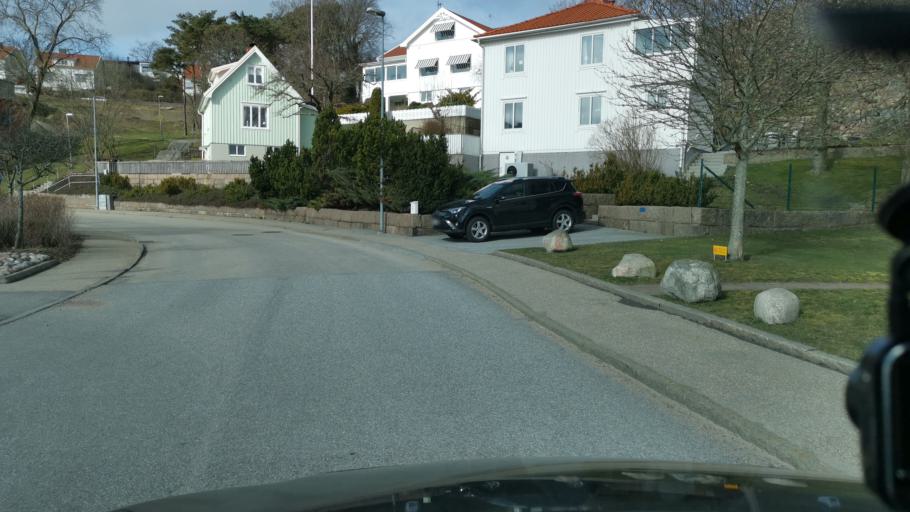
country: SE
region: Vaestra Goetaland
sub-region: Lysekils Kommun
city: Lysekil
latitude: 58.2768
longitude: 11.4413
